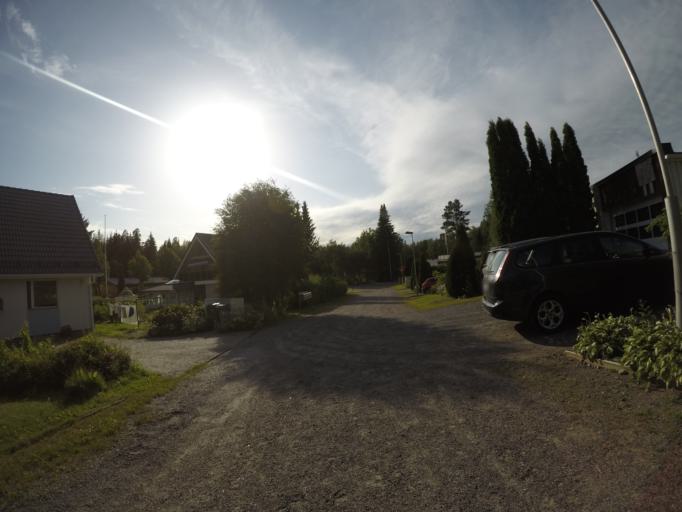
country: FI
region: Haeme
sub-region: Haemeenlinna
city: Haemeenlinna
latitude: 60.9767
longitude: 24.3903
